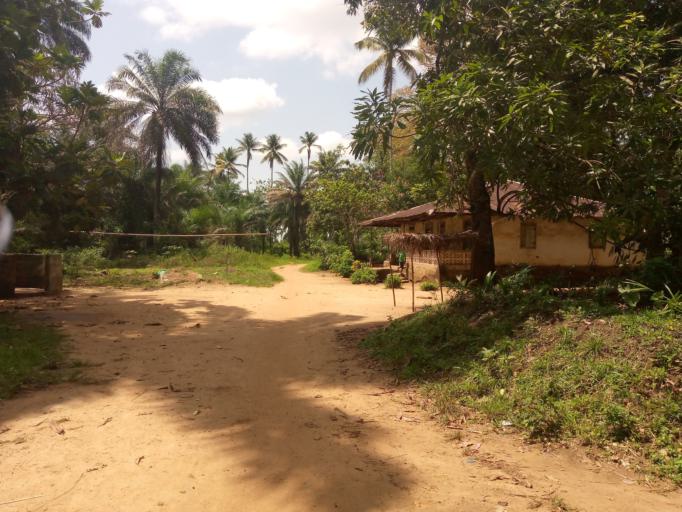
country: SL
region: Western Area
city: Waterloo
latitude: 8.3594
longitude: -12.9267
